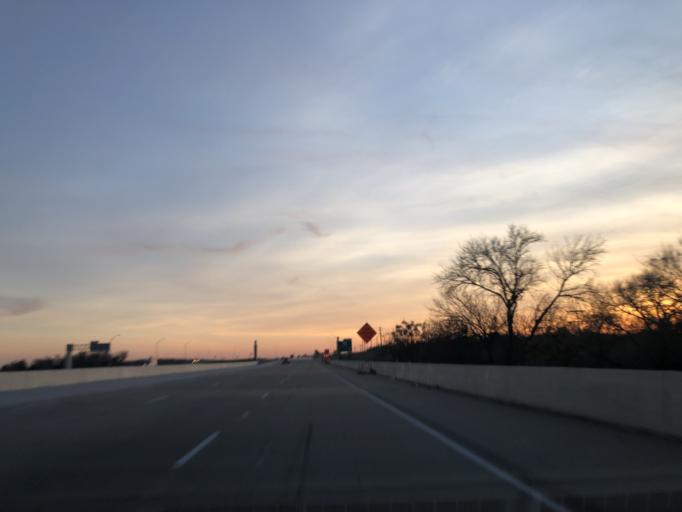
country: US
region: Texas
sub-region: Travis County
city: Manor
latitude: 30.3604
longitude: -97.5875
